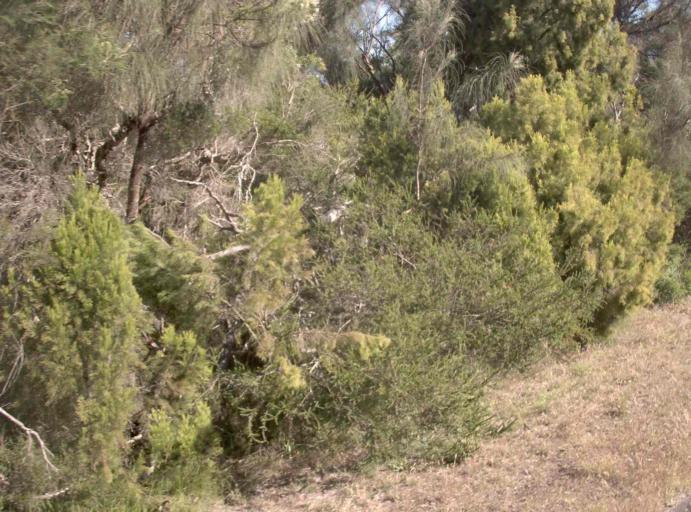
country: AU
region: Victoria
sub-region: Latrobe
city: Traralgon
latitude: -38.6365
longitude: 146.6740
